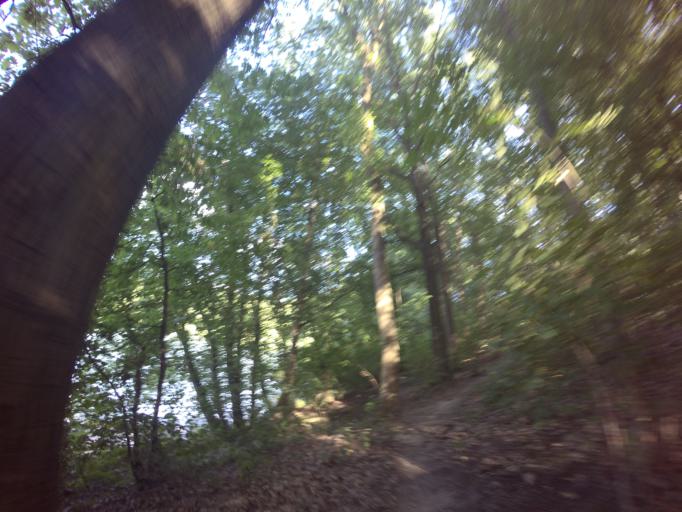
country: PL
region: West Pomeranian Voivodeship
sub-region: Powiat choszczenski
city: Choszczno
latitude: 53.1444
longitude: 15.4487
